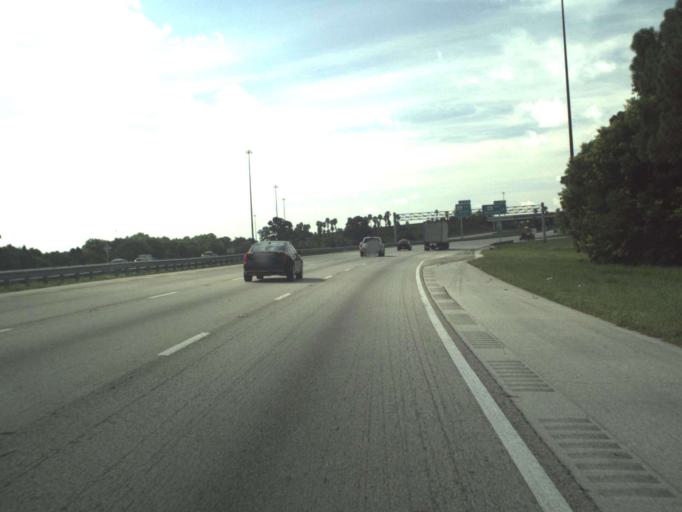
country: US
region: Florida
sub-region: Palm Beach County
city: Limestone Creek
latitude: 26.9418
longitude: -80.1529
